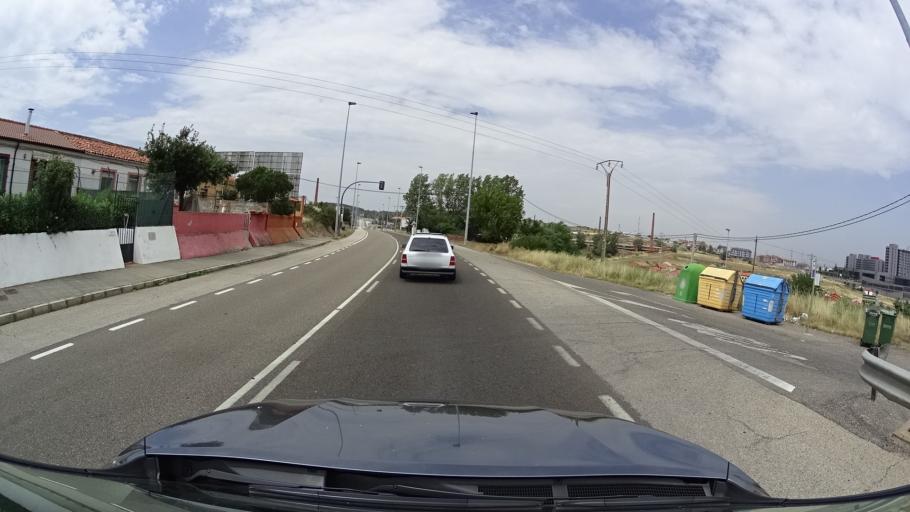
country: ES
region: Castille and Leon
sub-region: Provincia de Leon
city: Leon
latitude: 42.6150
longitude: -5.5782
